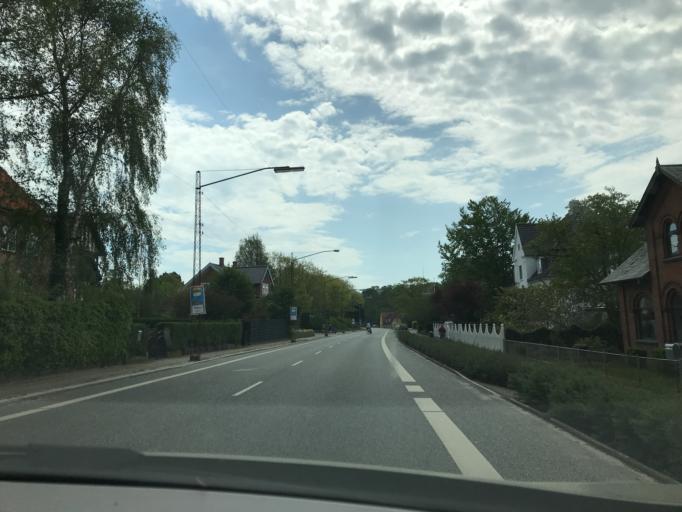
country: DK
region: South Denmark
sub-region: Assens Kommune
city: Assens
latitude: 55.2693
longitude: 9.9010
